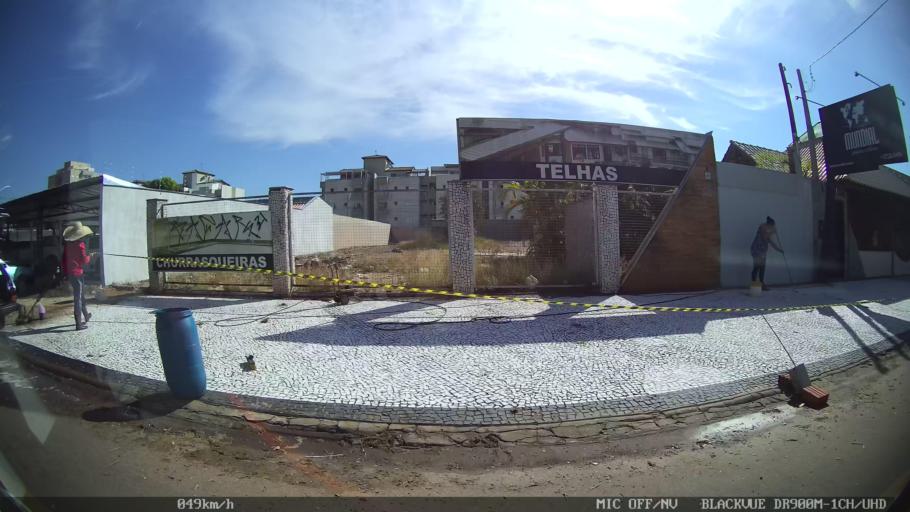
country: BR
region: Sao Paulo
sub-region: Franca
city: Franca
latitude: -20.5251
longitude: -47.4111
